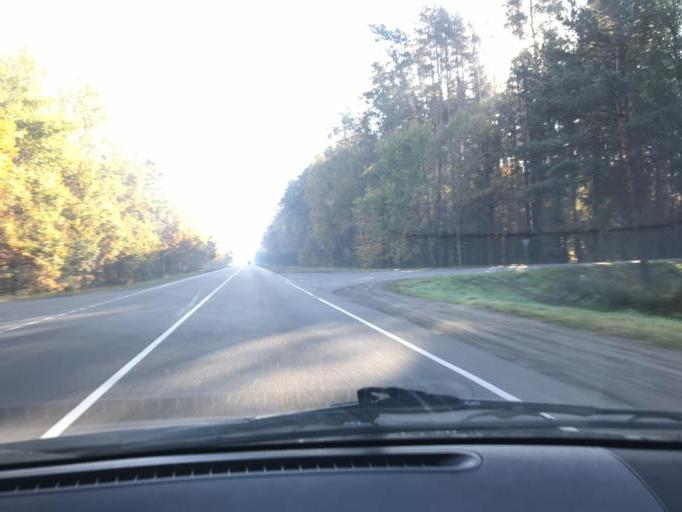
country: BY
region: Brest
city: Horad Luninyets
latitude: 52.2878
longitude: 26.7889
